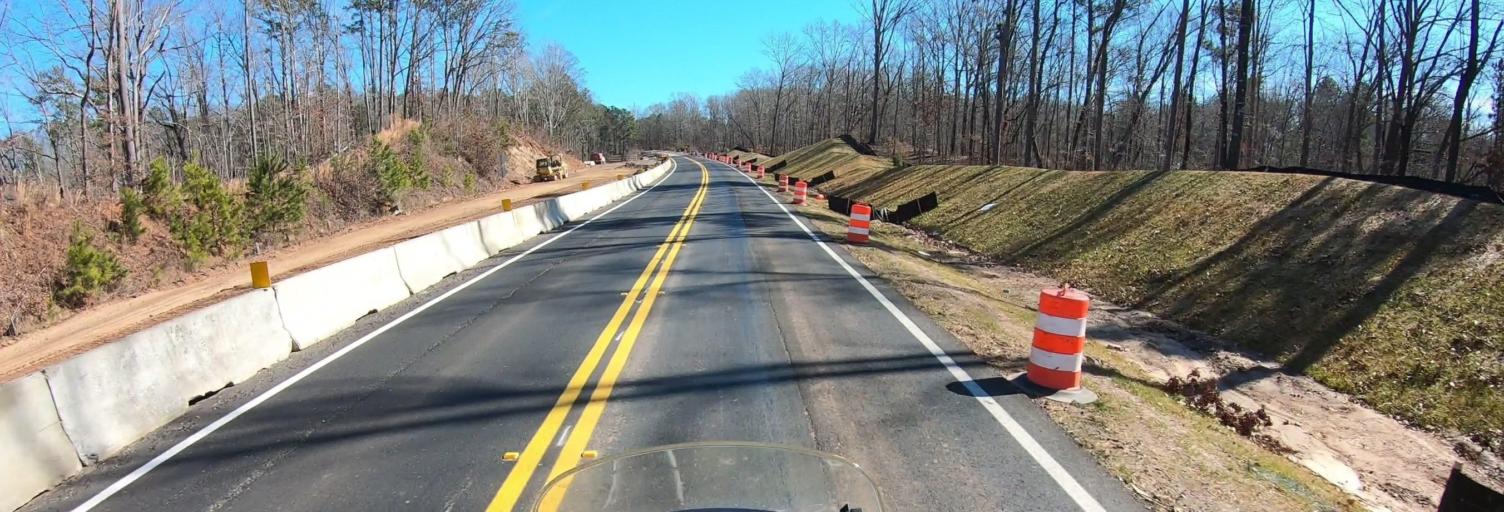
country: US
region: Georgia
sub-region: Hall County
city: Oakwood
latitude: 34.2605
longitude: -83.9480
